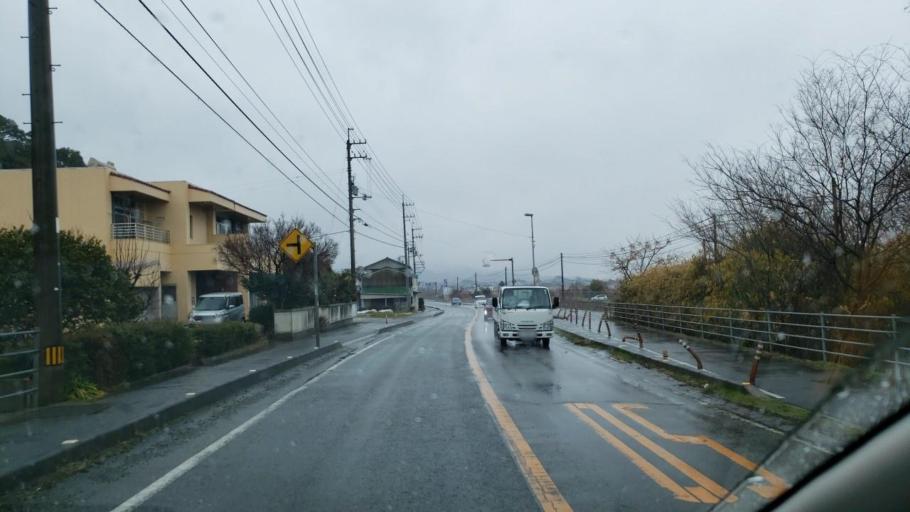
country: JP
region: Tokushima
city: Ishii
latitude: 34.1492
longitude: 134.4839
